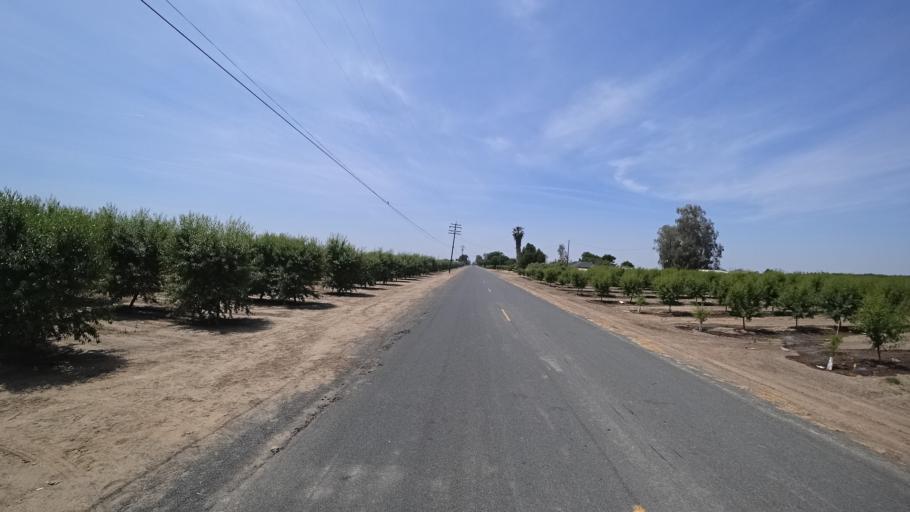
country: US
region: California
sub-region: Fresno County
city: Riverdale
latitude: 36.3948
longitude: -119.8209
